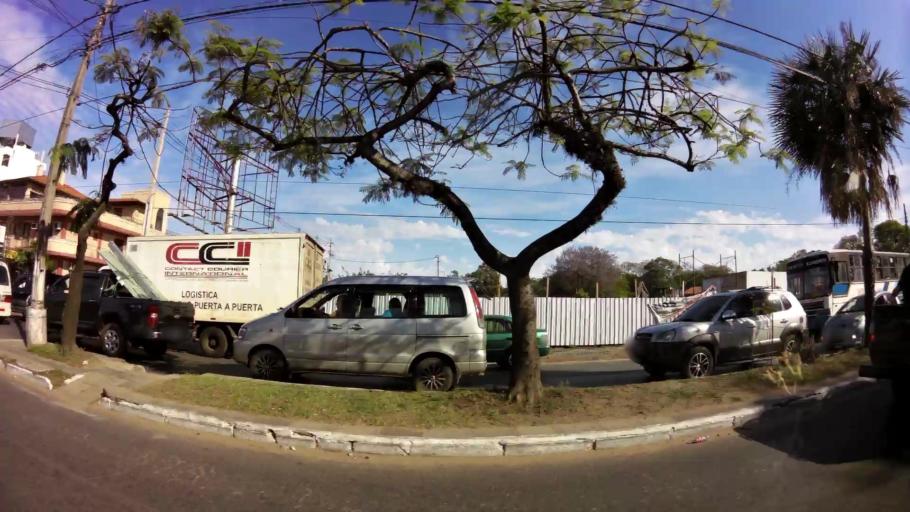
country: PY
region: Asuncion
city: Asuncion
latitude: -25.2525
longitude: -57.5789
